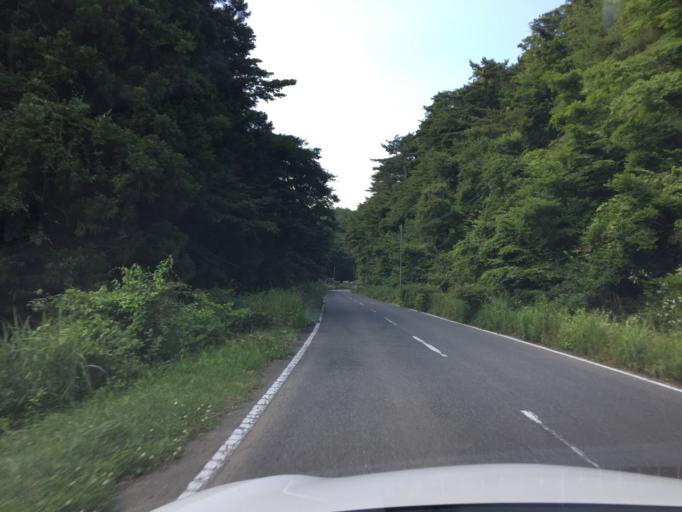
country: JP
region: Fukushima
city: Ishikawa
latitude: 37.1577
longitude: 140.6309
